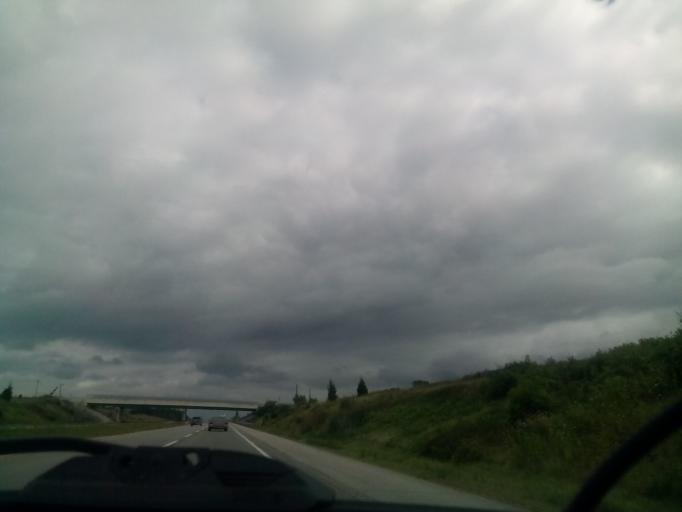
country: US
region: Indiana
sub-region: Steuben County
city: Fremont
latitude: 41.6825
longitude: -84.8805
